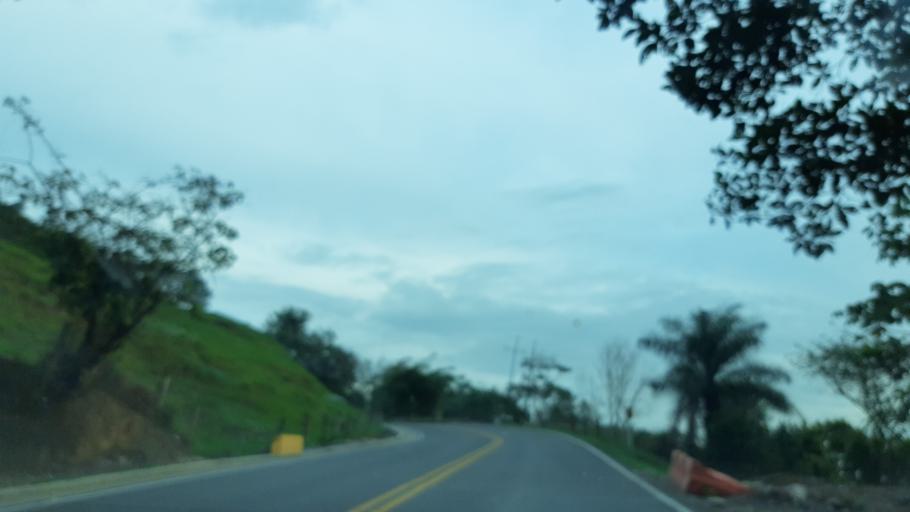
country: CO
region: Casanare
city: Sabanalarga
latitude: 4.7680
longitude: -73.0302
